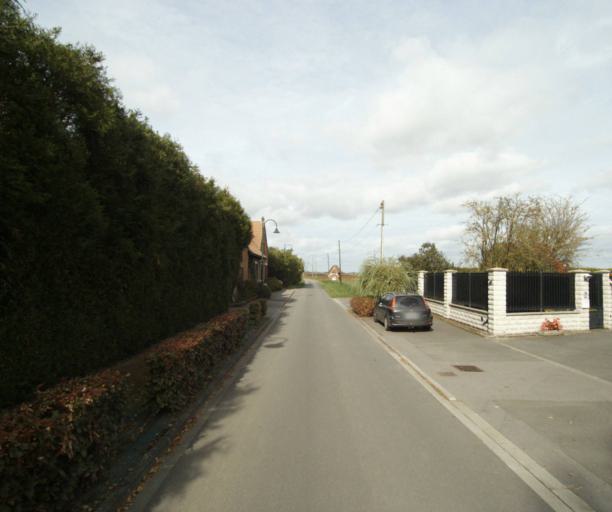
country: FR
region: Nord-Pas-de-Calais
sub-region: Departement du Nord
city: Bois-Grenier
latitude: 50.6509
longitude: 2.8688
